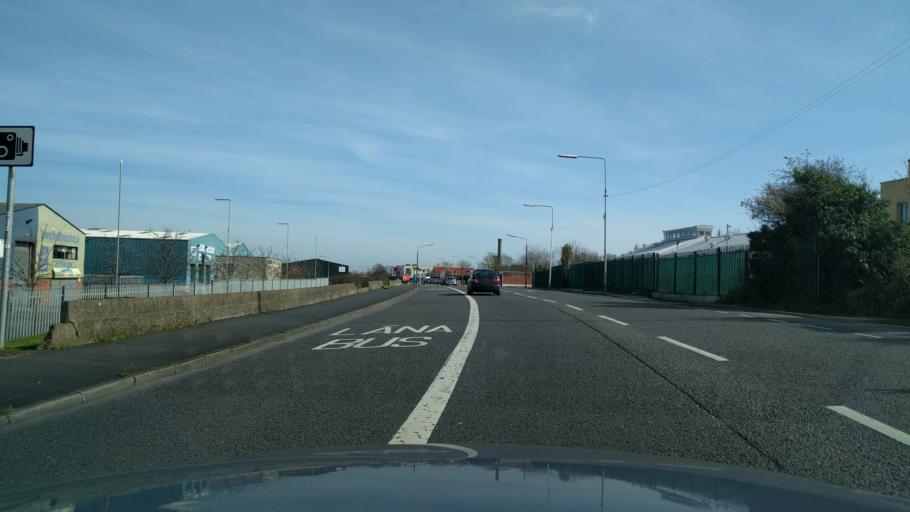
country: IE
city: Palmerstown
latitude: 53.3450
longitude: -6.3787
